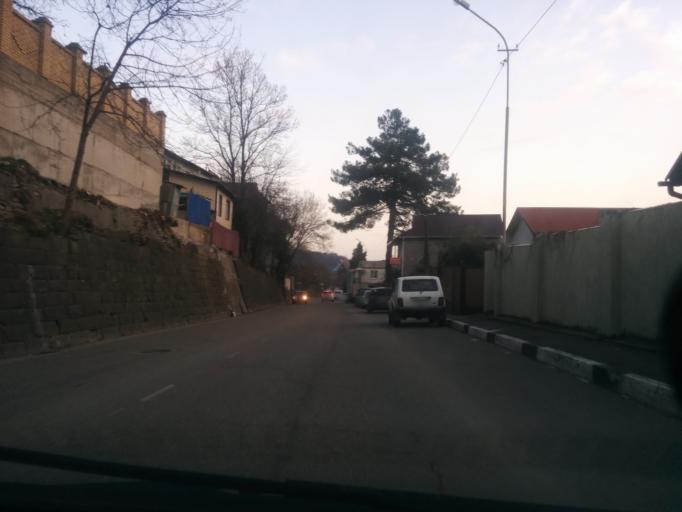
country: RU
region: Krasnodarskiy
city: Tuapse
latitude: 44.1031
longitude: 39.0691
